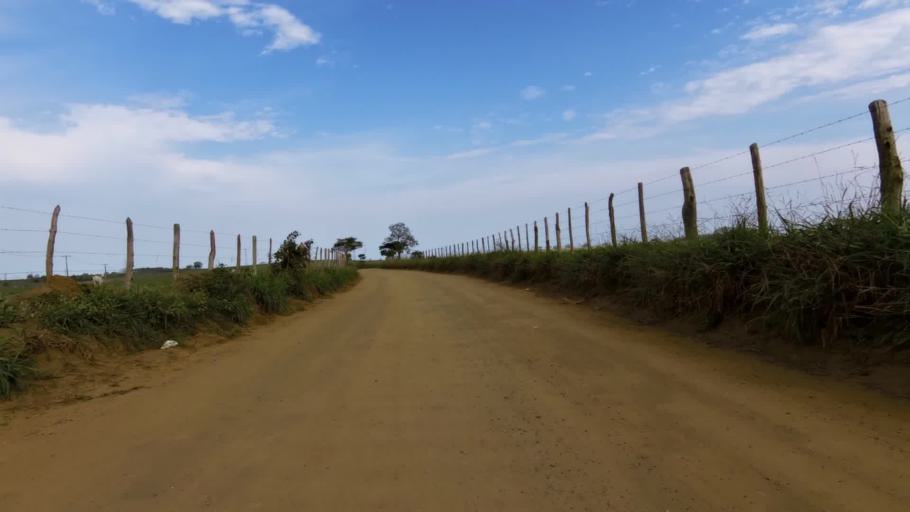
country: BR
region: Espirito Santo
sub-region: Piuma
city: Piuma
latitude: -20.8232
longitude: -40.7472
